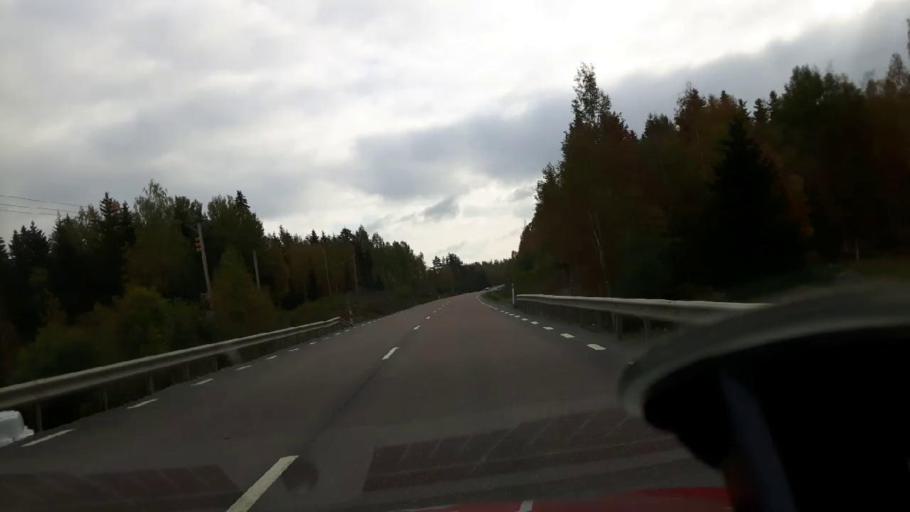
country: SE
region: Gaevleborg
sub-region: Bollnas Kommun
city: Kilafors
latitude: 61.2878
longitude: 16.5105
